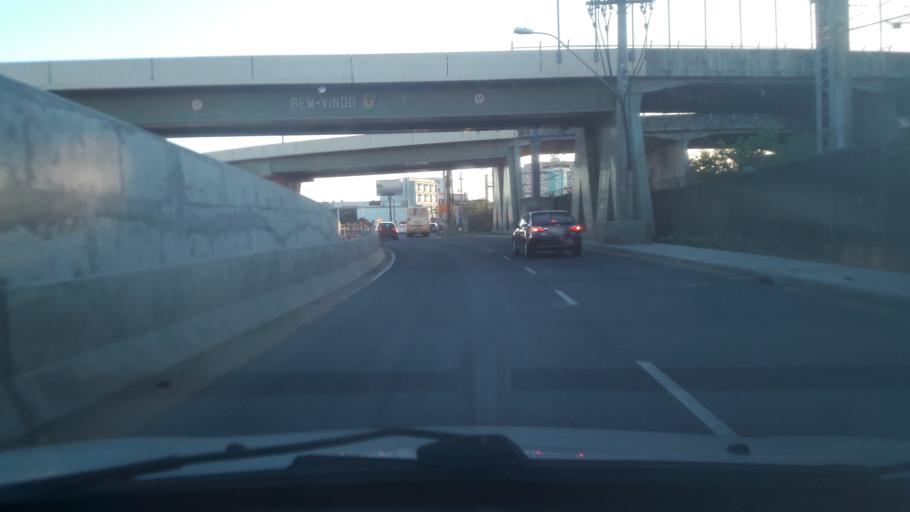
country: BR
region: Rio Grande do Sul
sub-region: Porto Alegre
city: Porto Alegre
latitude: -29.9955
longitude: -51.1893
